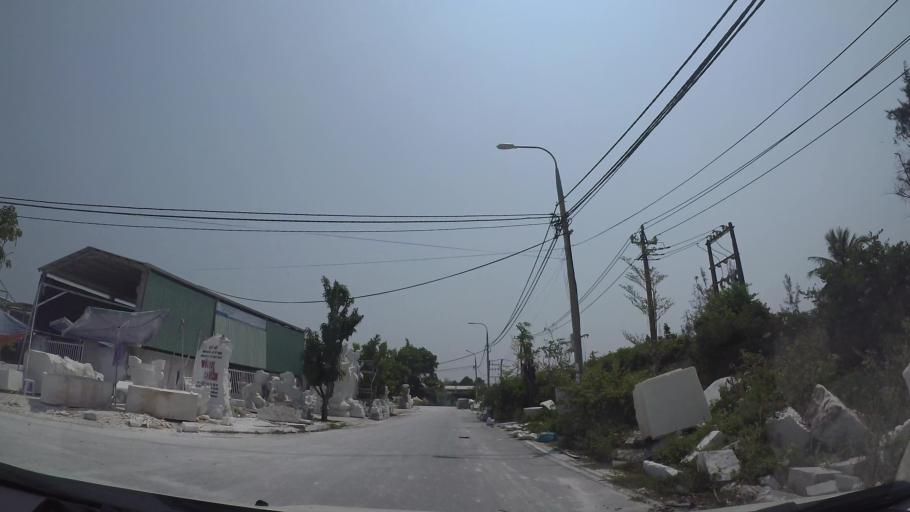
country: VN
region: Da Nang
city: Ngu Hanh Son
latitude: 15.9903
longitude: 108.2535
